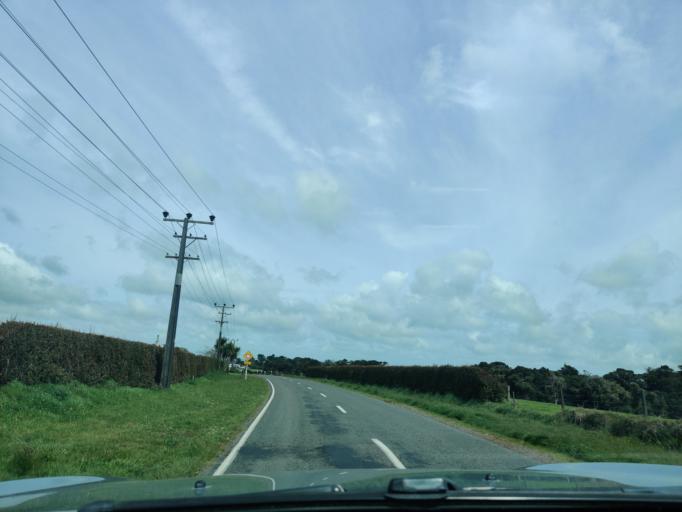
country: NZ
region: Taranaki
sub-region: South Taranaki District
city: Eltham
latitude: -39.3840
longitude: 174.1453
